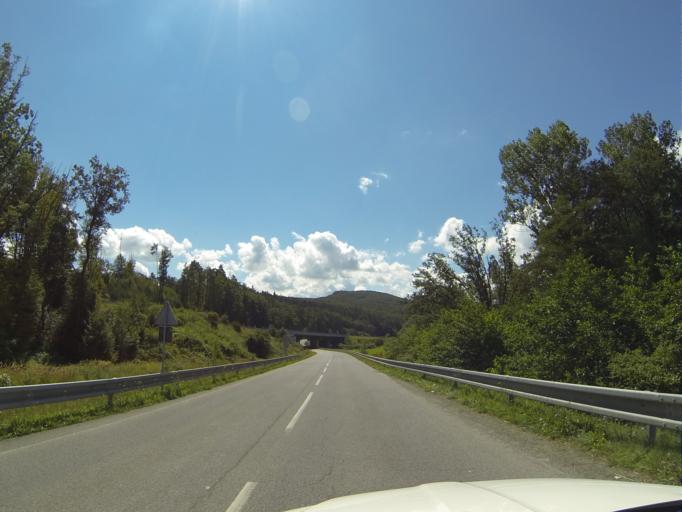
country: SK
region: Banskobystricky
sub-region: Okres Banska Bystrica
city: Zvolen
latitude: 48.5849
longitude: 19.0892
